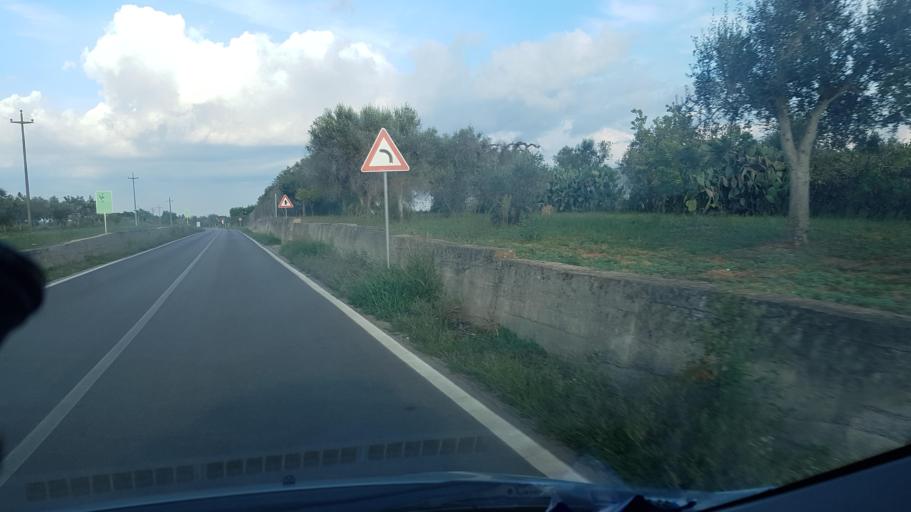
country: IT
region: Apulia
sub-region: Provincia di Lecce
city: Carmiano
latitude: 40.3411
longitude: 18.0106
